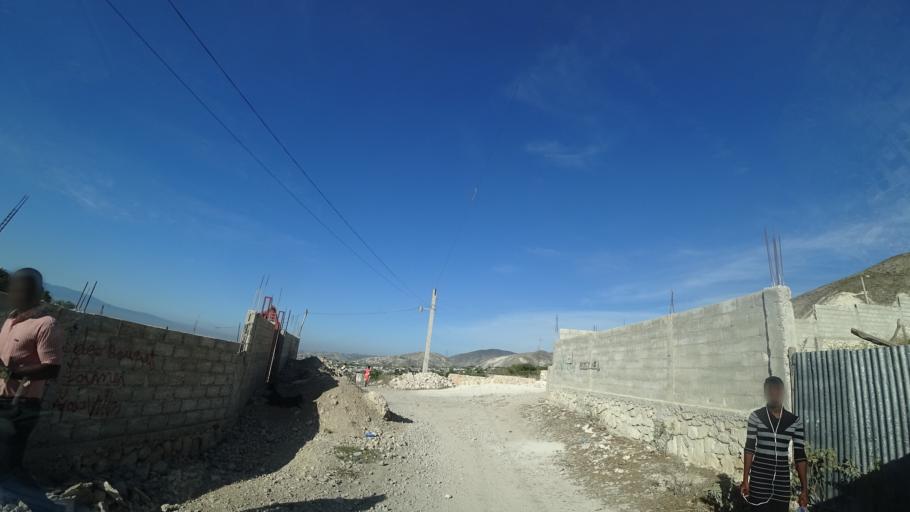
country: HT
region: Ouest
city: Croix des Bouquets
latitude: 18.6708
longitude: -72.2270
